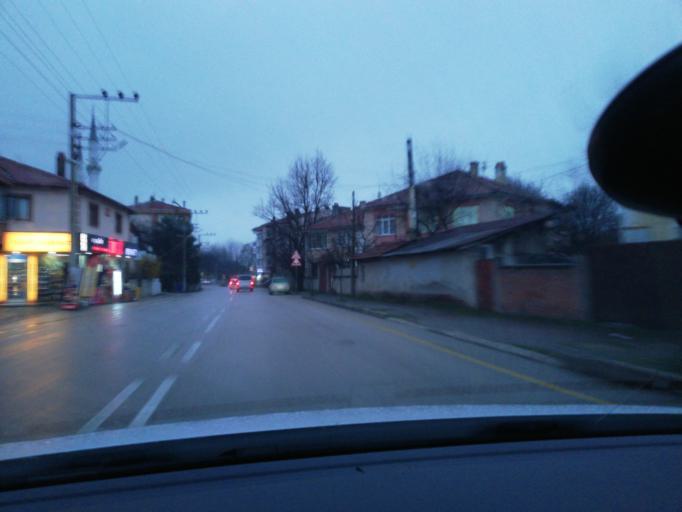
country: TR
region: Bolu
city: Bolu
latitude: 40.7300
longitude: 31.5763
